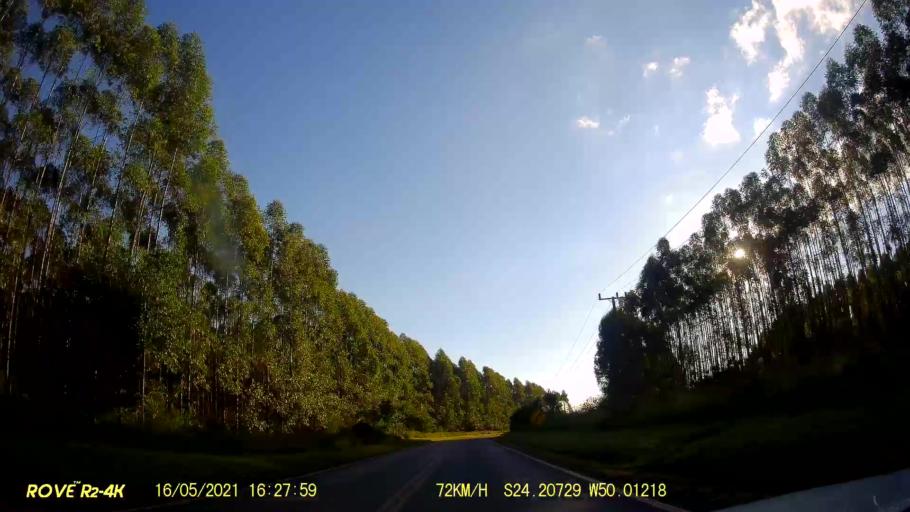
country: BR
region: Parana
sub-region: Jaguariaiva
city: Jaguariaiva
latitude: -24.2074
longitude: -50.0125
